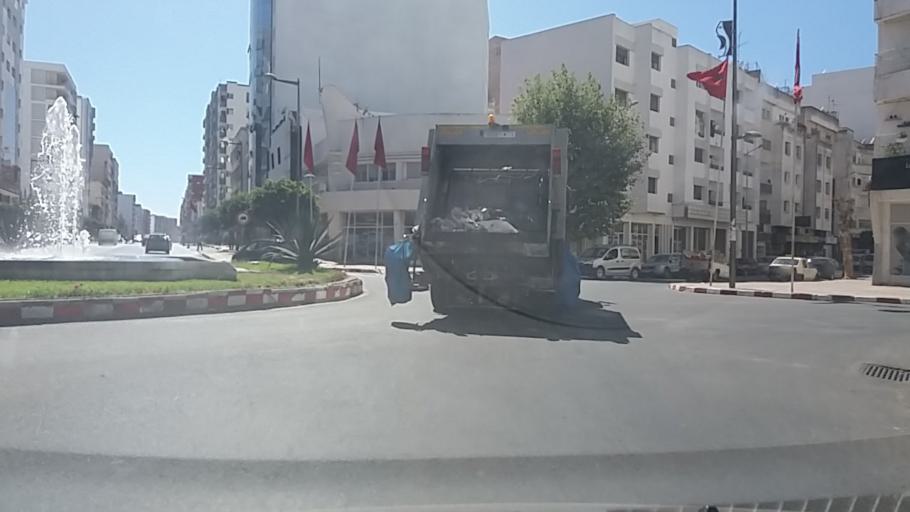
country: MA
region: Gharb-Chrarda-Beni Hssen
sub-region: Kenitra Province
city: Kenitra
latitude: 34.2587
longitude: -6.5869
